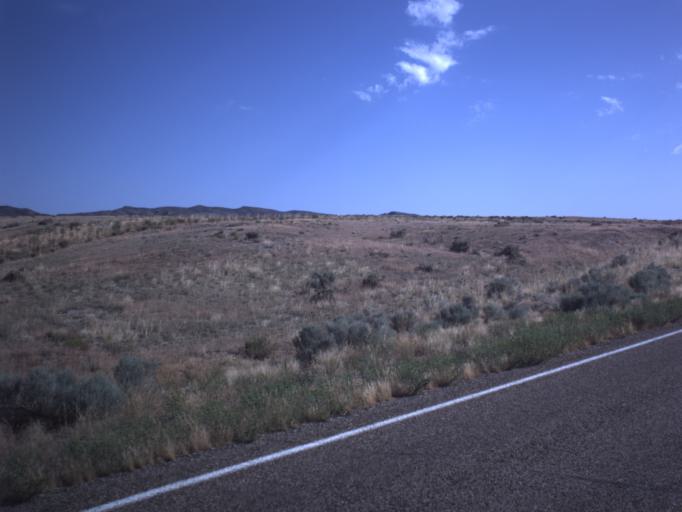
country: US
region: Utah
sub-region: Beaver County
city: Milford
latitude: 38.7719
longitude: -112.9329
